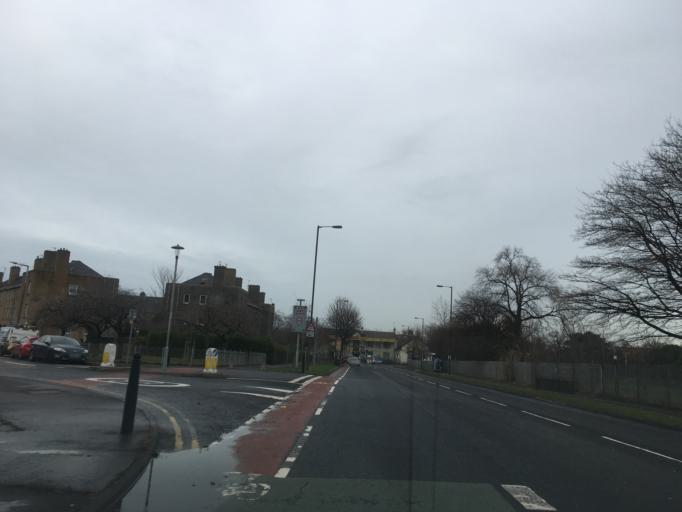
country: GB
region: Scotland
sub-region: Edinburgh
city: Colinton
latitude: 55.9364
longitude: -3.2512
